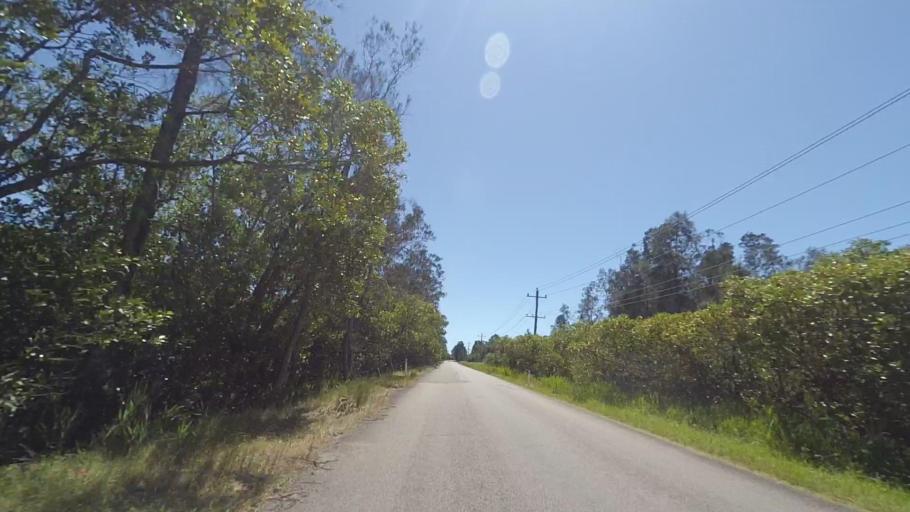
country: AU
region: New South Wales
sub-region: Port Stephens Shire
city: Medowie
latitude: -32.7850
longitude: 151.9391
